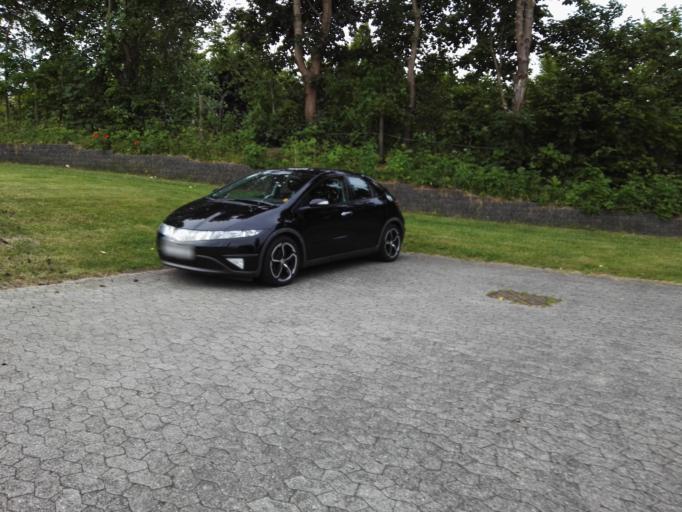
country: DK
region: Capital Region
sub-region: Ballerup Kommune
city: Ballerup
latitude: 55.7458
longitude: 12.3702
